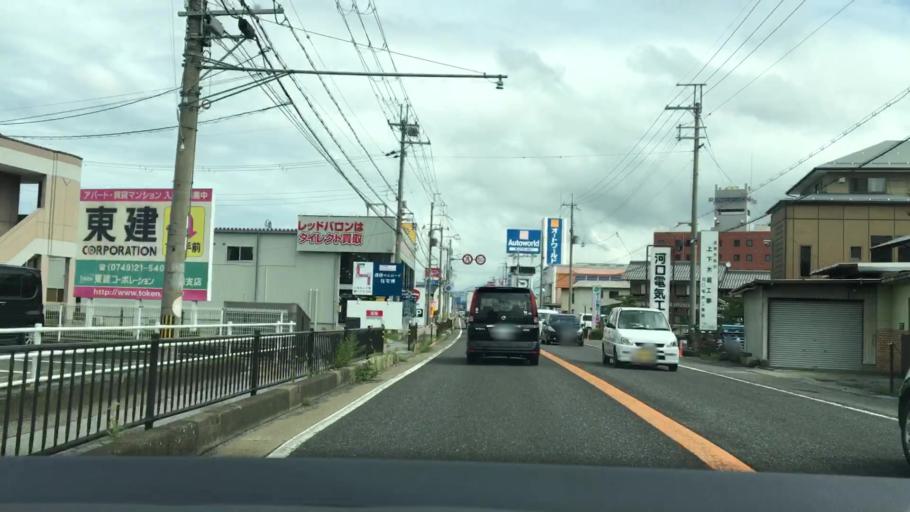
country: JP
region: Shiga Prefecture
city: Hikone
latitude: 35.2381
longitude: 136.2537
